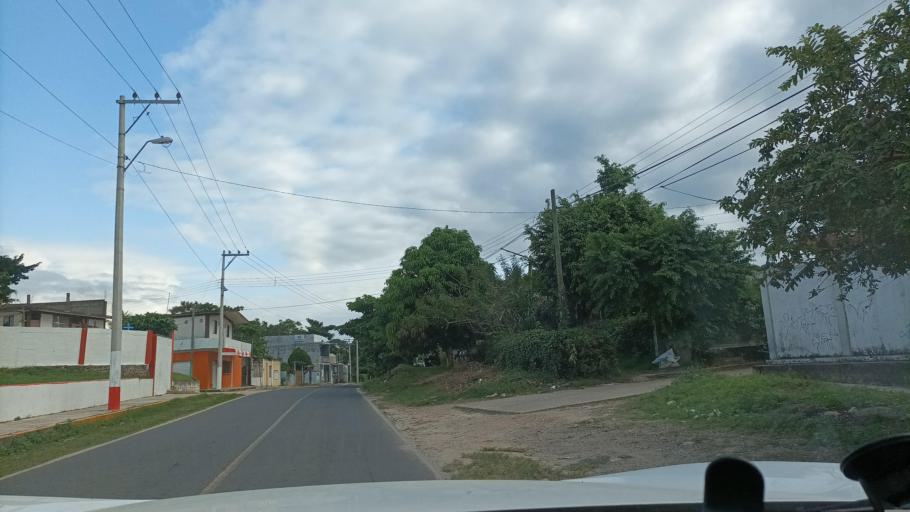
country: MX
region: Veracruz
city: Oluta
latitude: 17.9249
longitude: -94.8891
